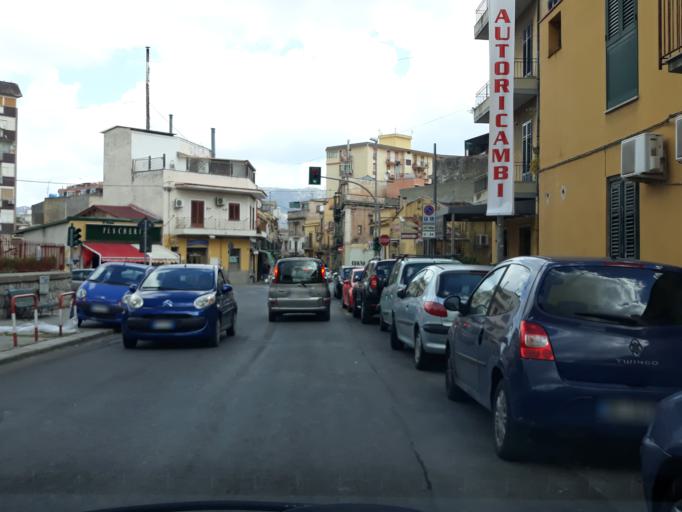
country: IT
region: Sicily
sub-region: Palermo
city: Palermo
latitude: 38.1255
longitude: 13.3126
